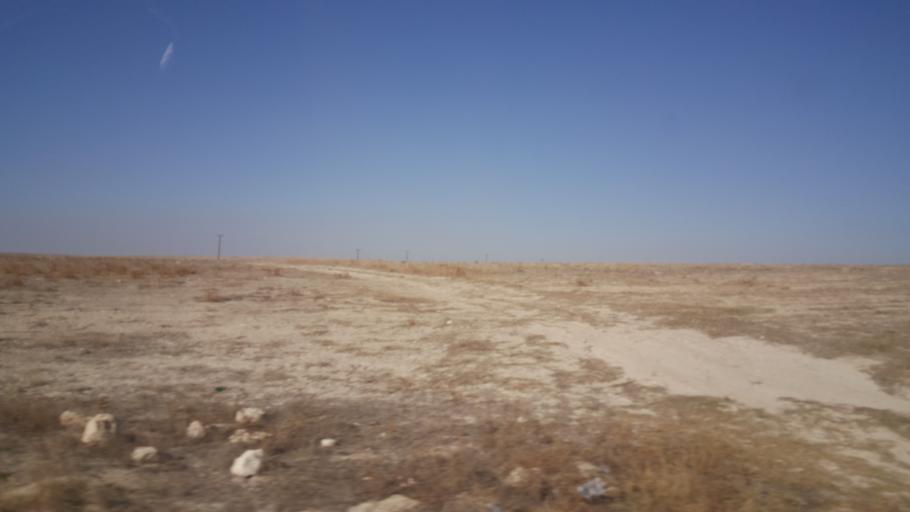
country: TR
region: Konya
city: Celtik
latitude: 39.0613
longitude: 31.8635
